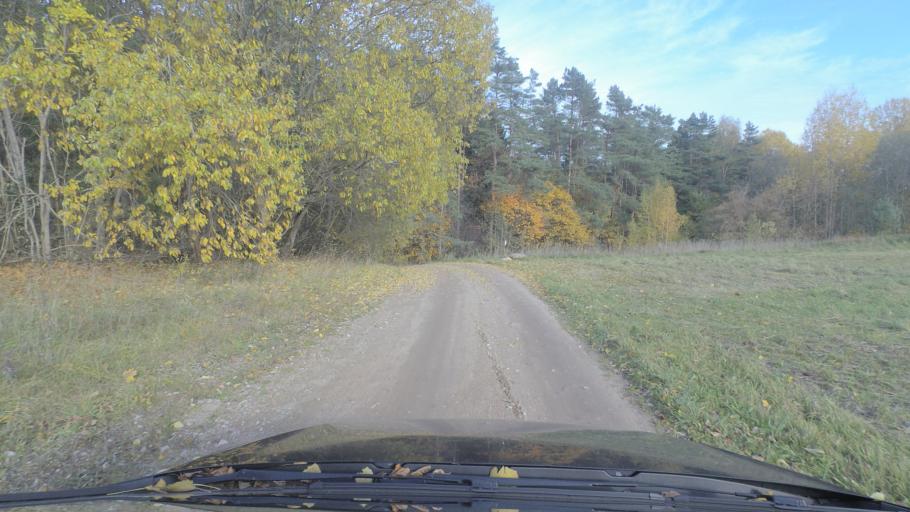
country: LT
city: Ignalina
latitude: 55.3356
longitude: 26.1772
